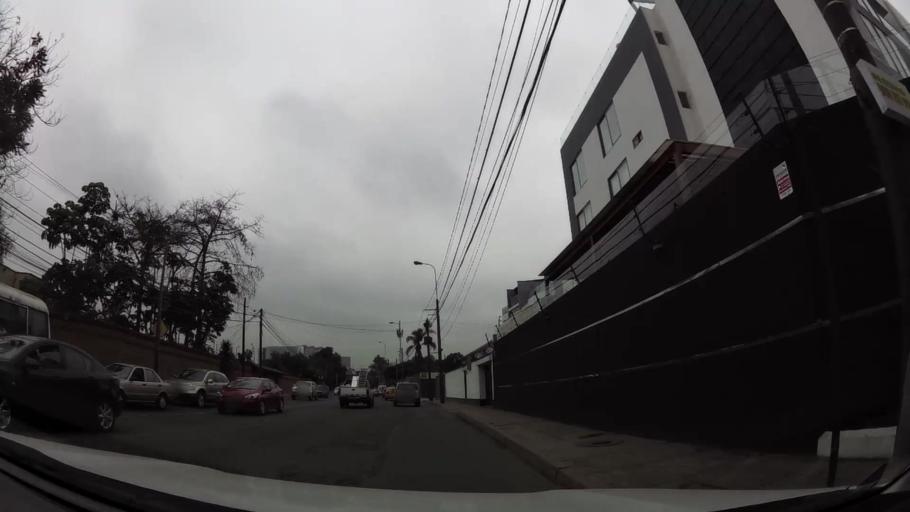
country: PE
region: Lima
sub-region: Lima
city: La Molina
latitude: -12.0917
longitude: -76.9671
